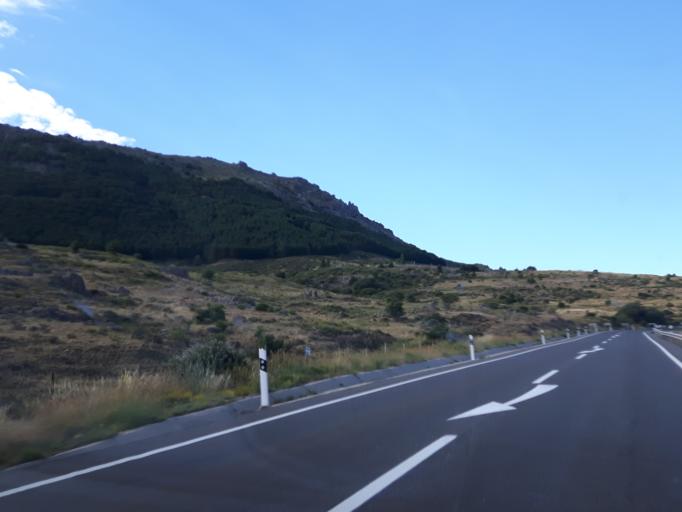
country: ES
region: Castille and Leon
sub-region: Provincia de Avila
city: Mengamunoz
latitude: 40.4928
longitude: -5.0056
